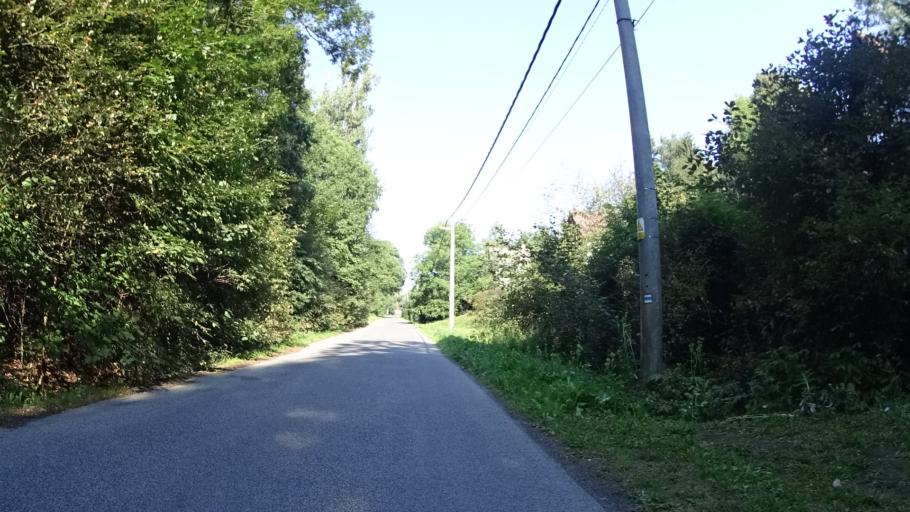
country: CZ
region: Liberecky
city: Hodkovice nad Mohelkou
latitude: 50.6951
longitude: 15.1025
